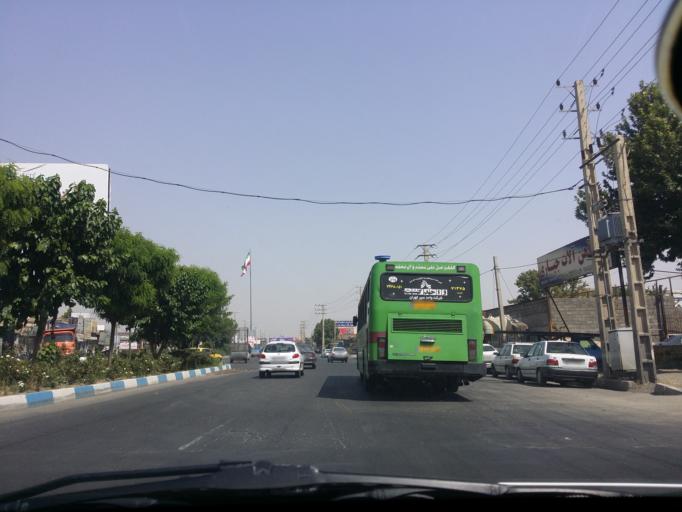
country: IR
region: Alborz
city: Karaj
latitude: 35.8541
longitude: 50.8985
